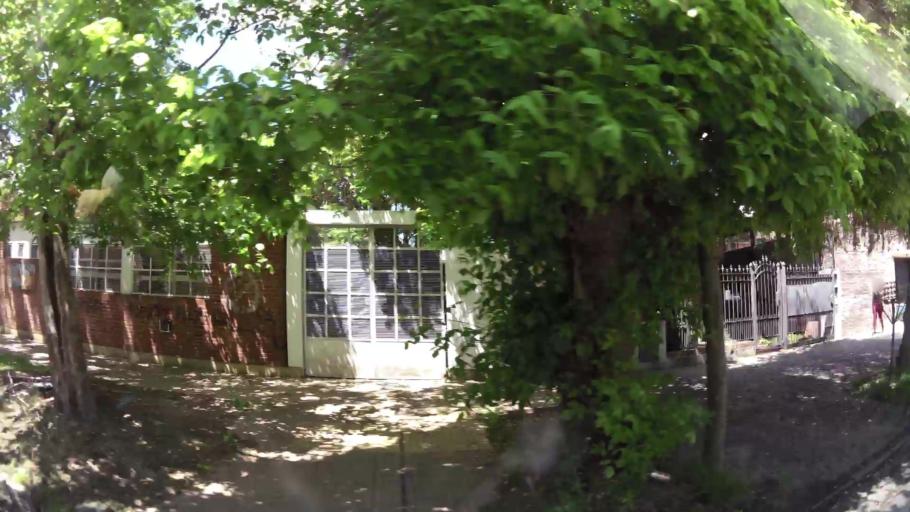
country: AR
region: Buenos Aires
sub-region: Partido de Lanus
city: Lanus
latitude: -34.7318
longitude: -58.3995
